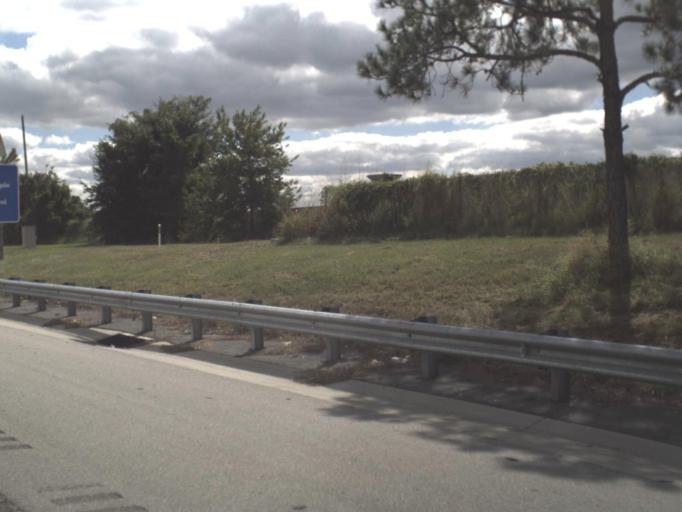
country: US
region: Florida
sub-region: Orange County
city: Gotha
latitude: 28.5268
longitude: -81.5159
